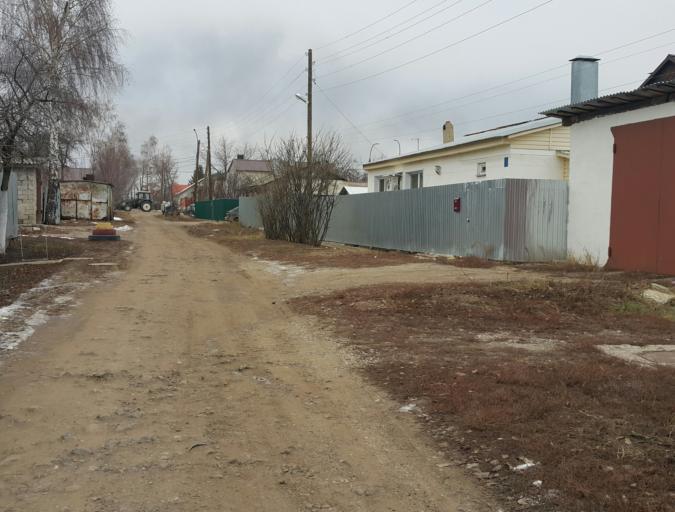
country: RU
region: Tambov
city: Tambov
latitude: 52.7235
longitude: 41.4020
